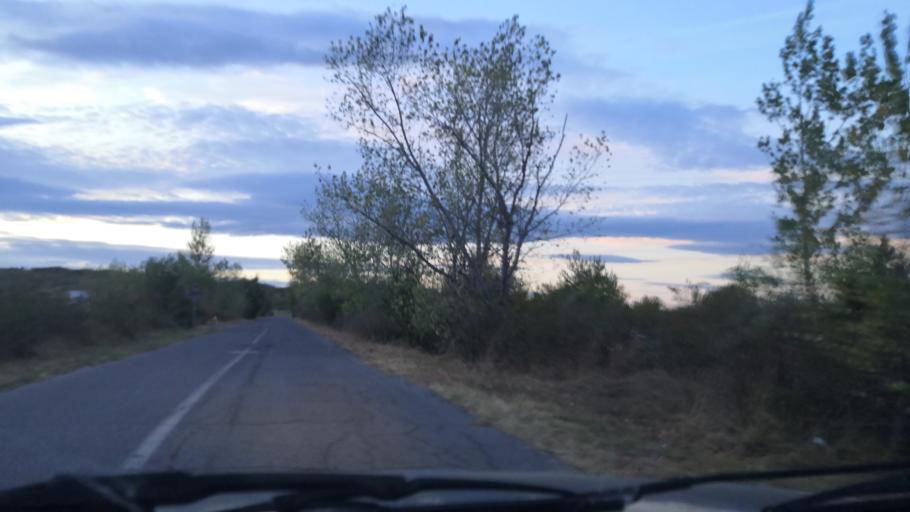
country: RO
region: Mehedinti
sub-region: Comuna Gogosu
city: Balta Verde
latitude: 44.2967
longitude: 22.5551
